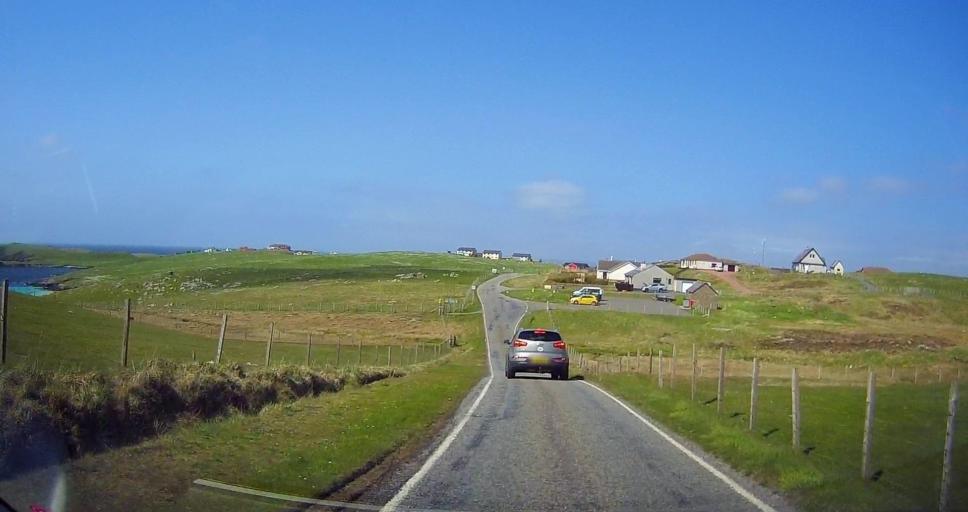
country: GB
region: Scotland
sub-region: Shetland Islands
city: Sandwick
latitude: 60.1014
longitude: -1.3222
